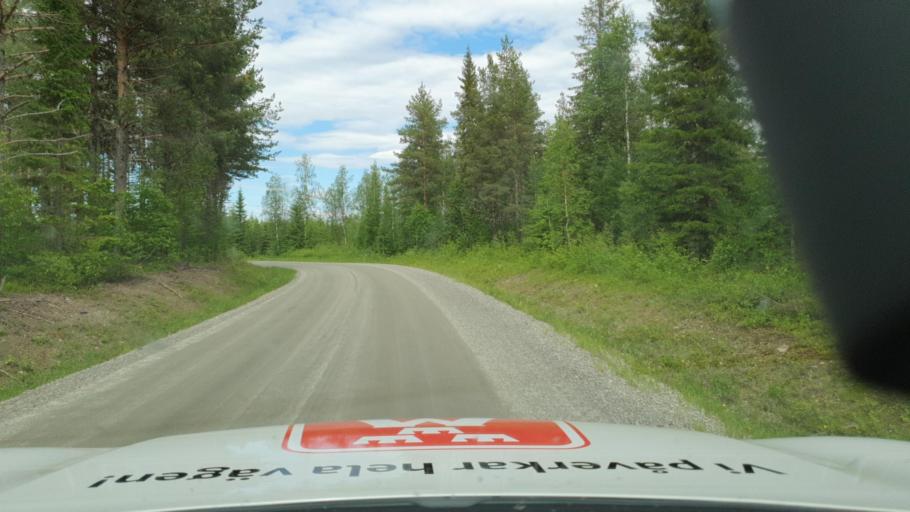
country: SE
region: Vaesterbotten
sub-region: Norsjo Kommun
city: Norsjoe
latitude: 64.8229
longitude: 19.6971
